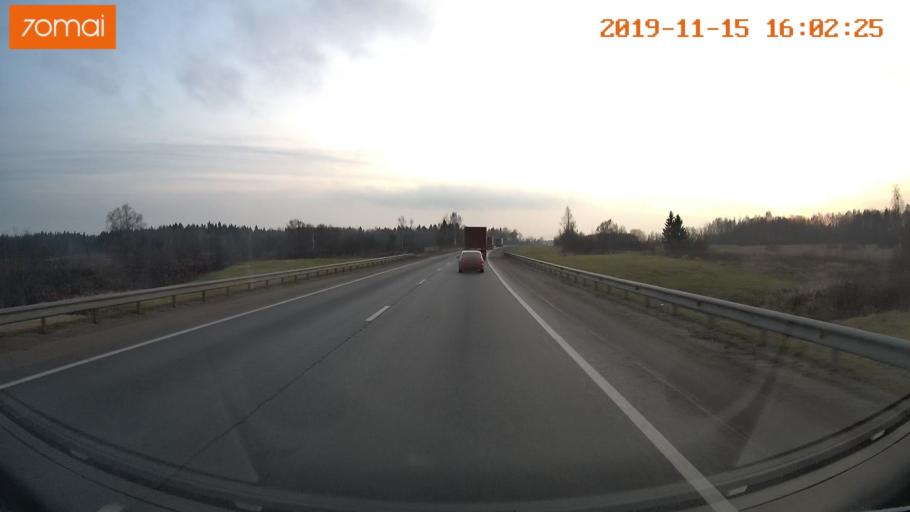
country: RU
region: Jaroslavl
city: Yaroslavl
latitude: 57.7717
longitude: 39.9246
